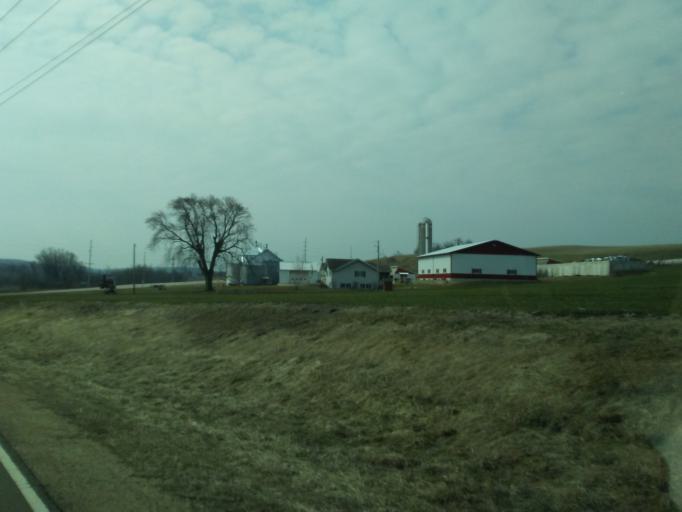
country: US
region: Wisconsin
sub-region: Columbia County
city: Lodi
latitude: 43.3052
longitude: -89.5416
